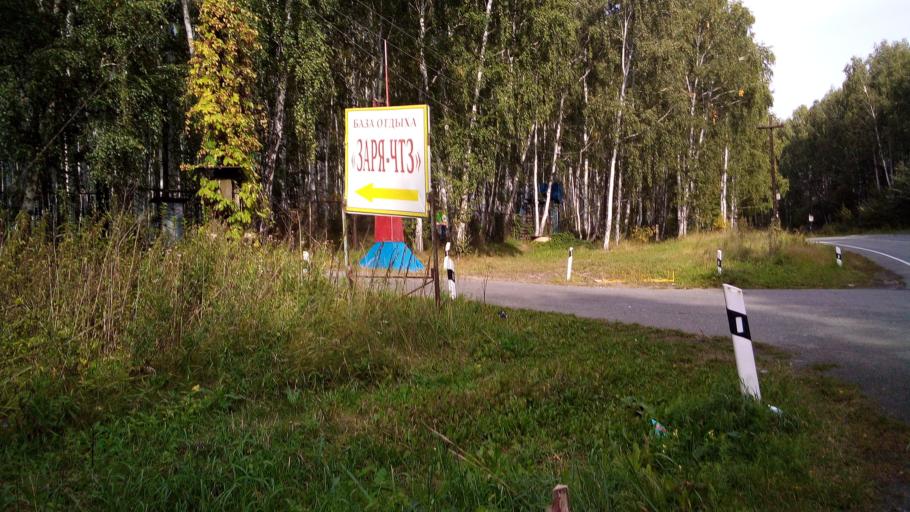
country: RU
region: Chelyabinsk
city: Tayginka
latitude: 55.4746
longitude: 60.4913
